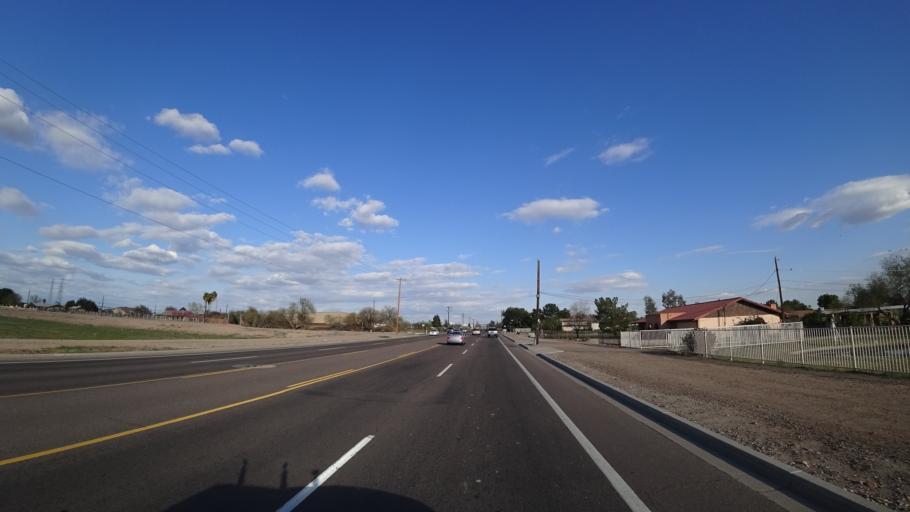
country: US
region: Arizona
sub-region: Maricopa County
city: Peoria
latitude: 33.5519
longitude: -112.2435
